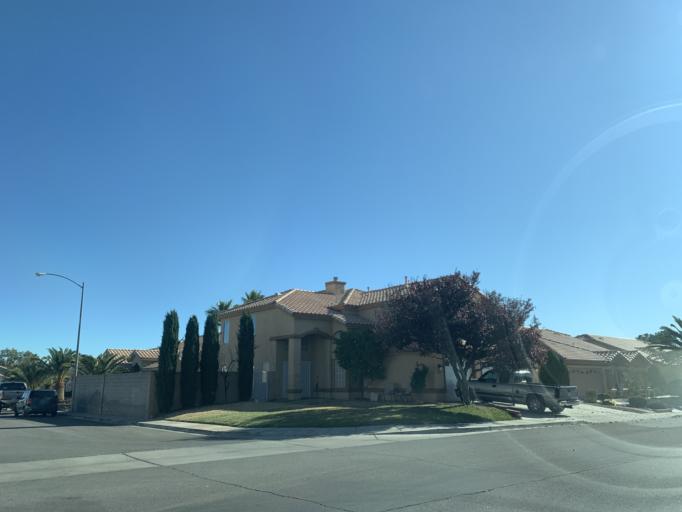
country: US
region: Nevada
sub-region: Clark County
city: Summerlin South
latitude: 36.1201
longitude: -115.2903
